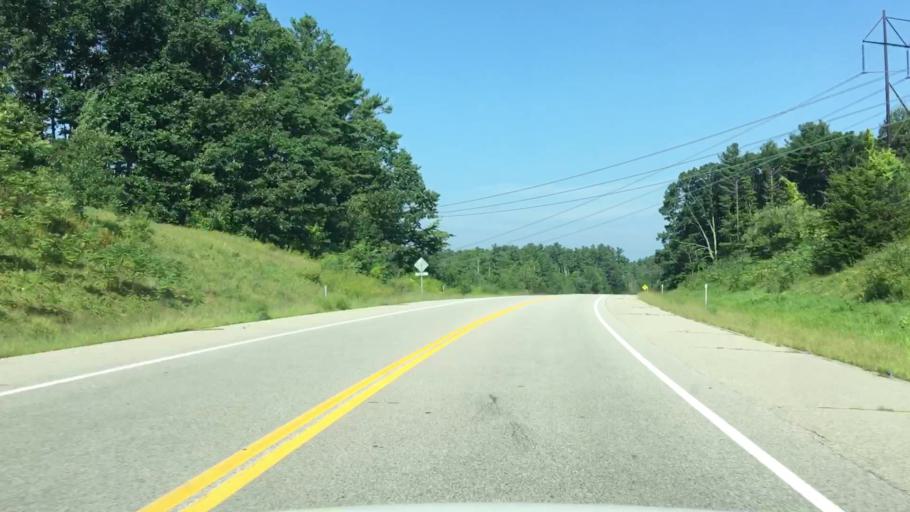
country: US
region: New Hampshire
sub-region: Rockingham County
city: Seabrook
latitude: 42.8994
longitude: -70.9057
